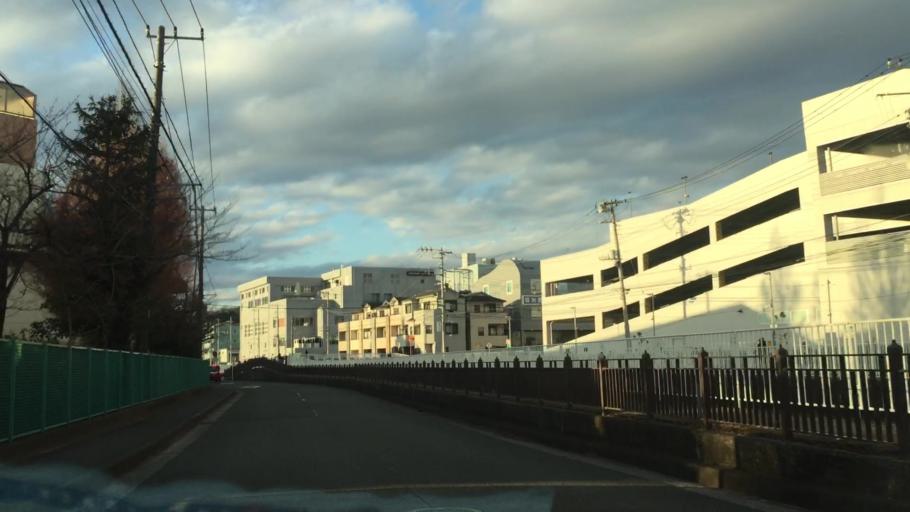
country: JP
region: Kanagawa
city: Zushi
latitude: 35.3416
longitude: 139.6191
